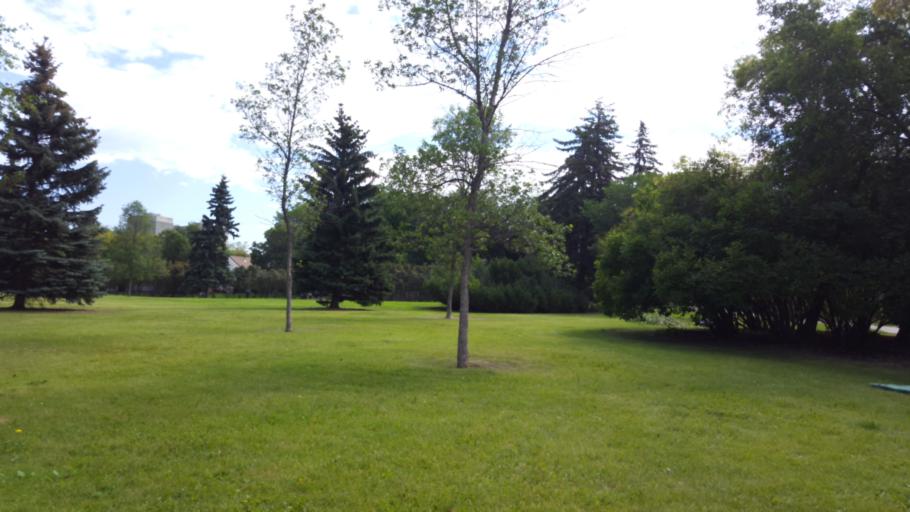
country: CA
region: Alberta
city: Edmonton
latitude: 53.5148
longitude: -113.5302
